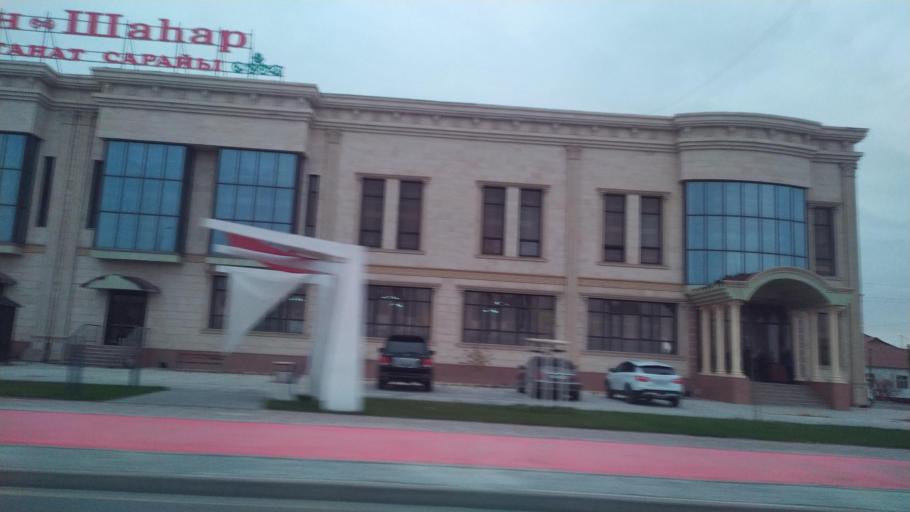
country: KZ
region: Ongtustik Qazaqstan
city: Turkestan
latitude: 43.2800
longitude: 68.3224
